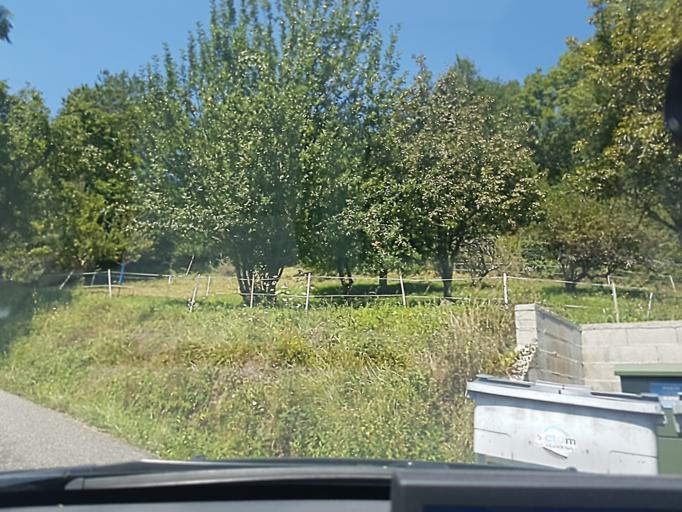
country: FR
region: Midi-Pyrenees
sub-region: Departement de l'Ariege
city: Saint-Girons
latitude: 42.8992
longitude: 1.3304
